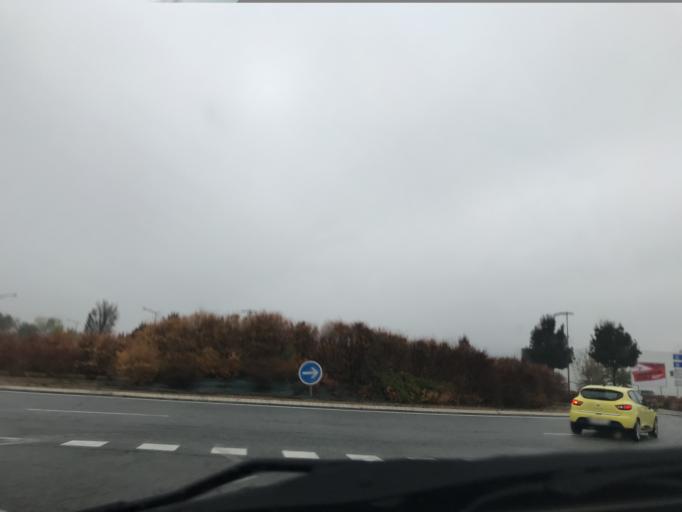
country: FR
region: Auvergne
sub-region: Departement du Puy-de-Dome
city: Aulnat
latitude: 45.7769
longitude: 3.1876
